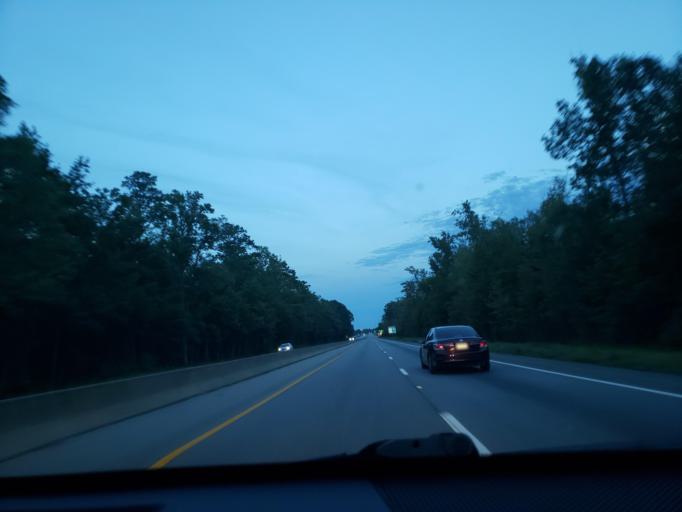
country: US
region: Virginia
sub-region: City of Franklin
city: Franklin
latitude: 36.6706
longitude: -76.9700
